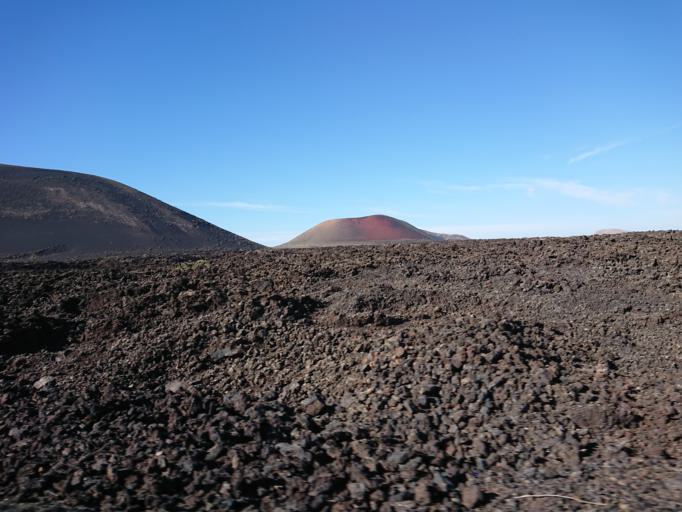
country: ES
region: Canary Islands
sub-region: Provincia de Las Palmas
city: Tias
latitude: 28.9914
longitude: -13.6694
